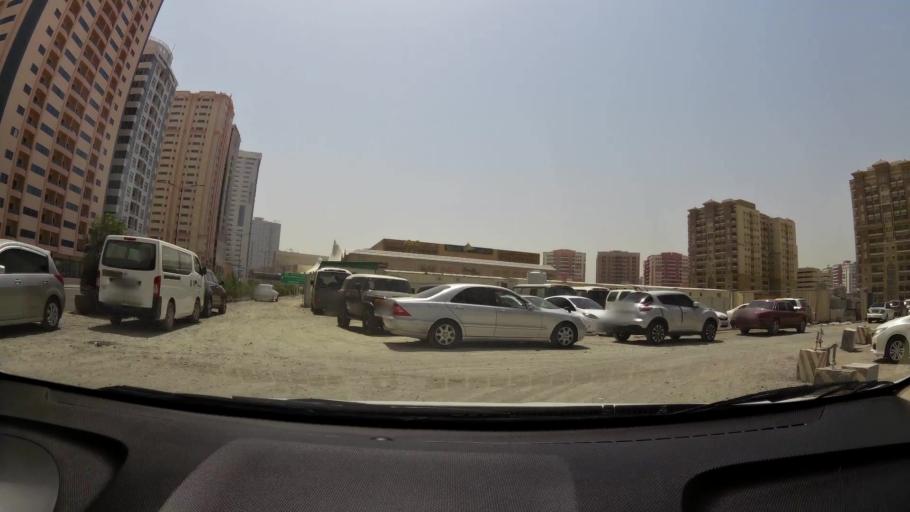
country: AE
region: Ash Shariqah
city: Sharjah
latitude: 25.2984
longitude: 55.3687
